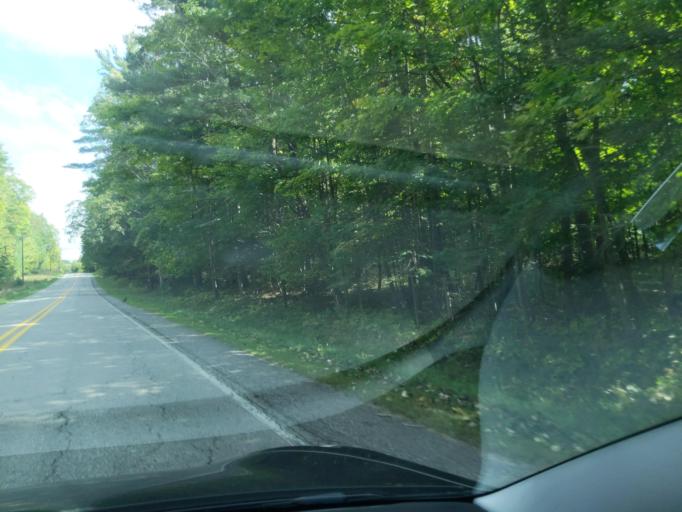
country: US
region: Michigan
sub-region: Antrim County
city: Bellaire
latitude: 45.0492
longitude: -85.3115
